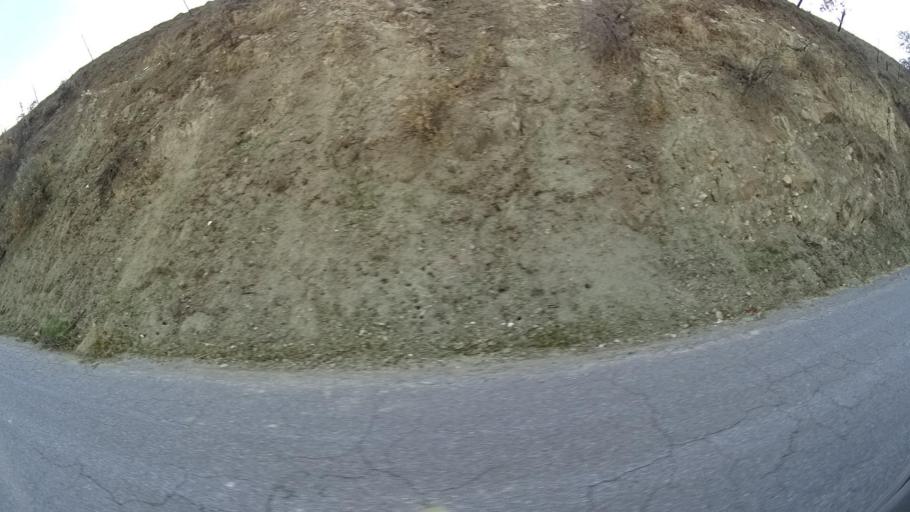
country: US
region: California
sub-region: Kern County
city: Bear Valley Springs
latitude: 35.2860
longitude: -118.6643
